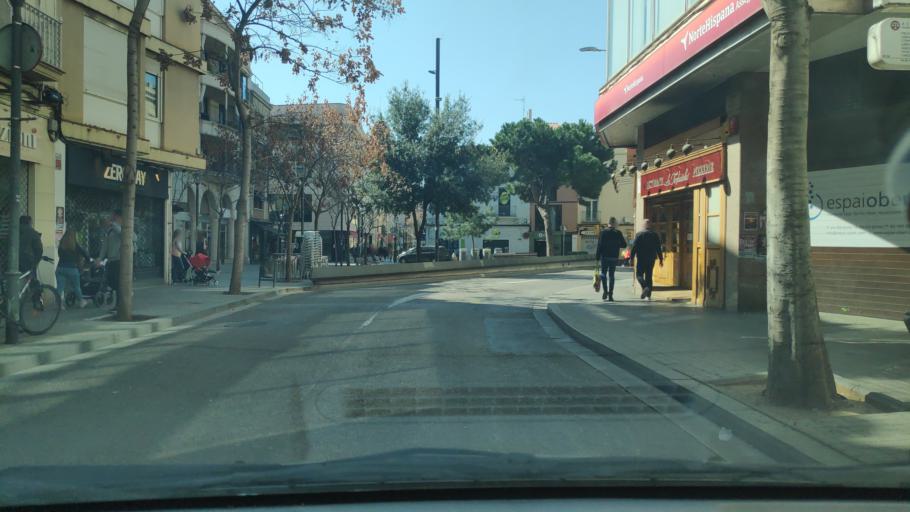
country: ES
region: Catalonia
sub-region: Provincia de Barcelona
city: Sabadell
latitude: 41.5485
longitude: 2.1073
